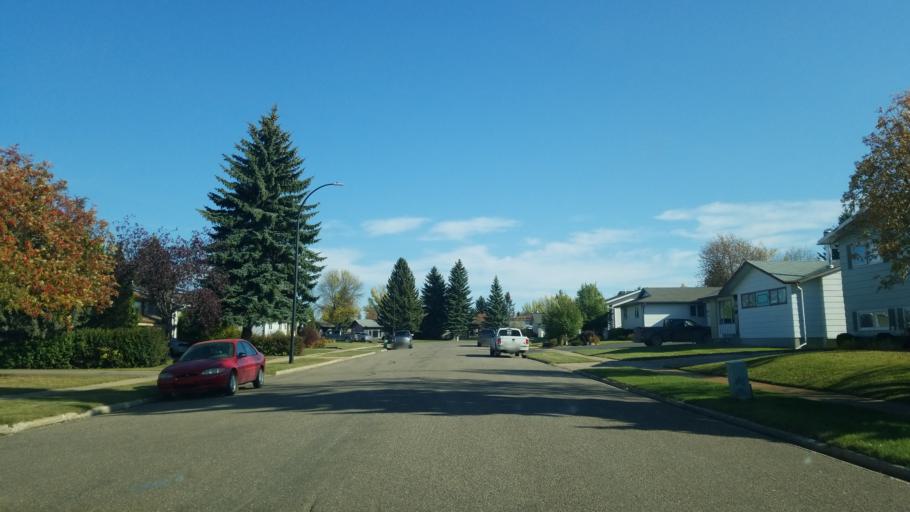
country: CA
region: Saskatchewan
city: Lloydminster
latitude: 53.2691
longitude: -110.0149
